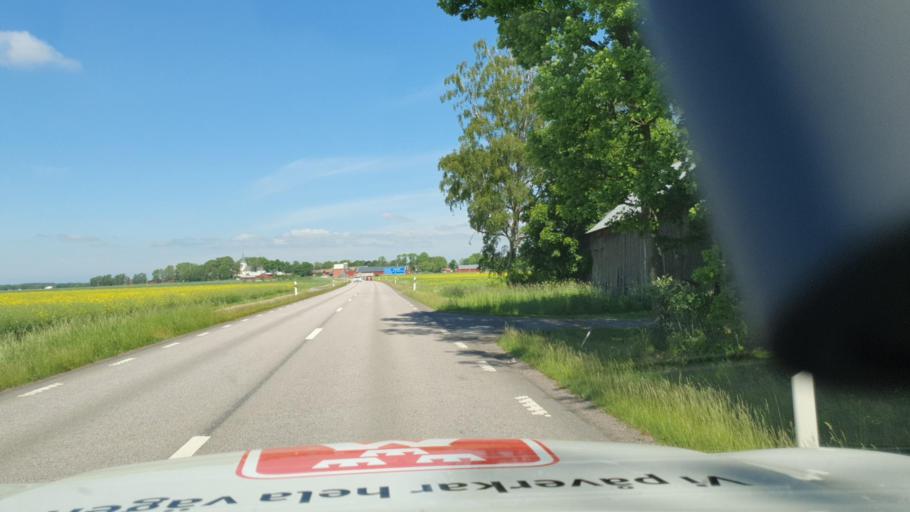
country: SE
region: Vaestra Goetaland
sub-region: Vara Kommun
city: Vara
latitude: 58.2898
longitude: 12.9607
